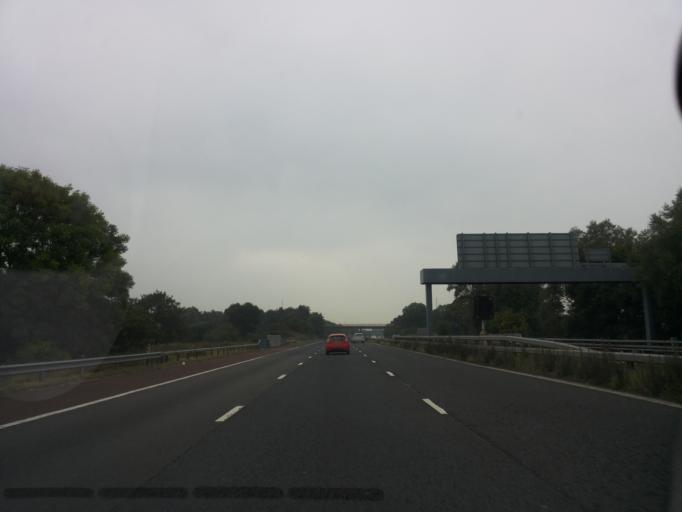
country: GB
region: England
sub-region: Lancashire
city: Preston
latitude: 53.7993
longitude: -2.7283
